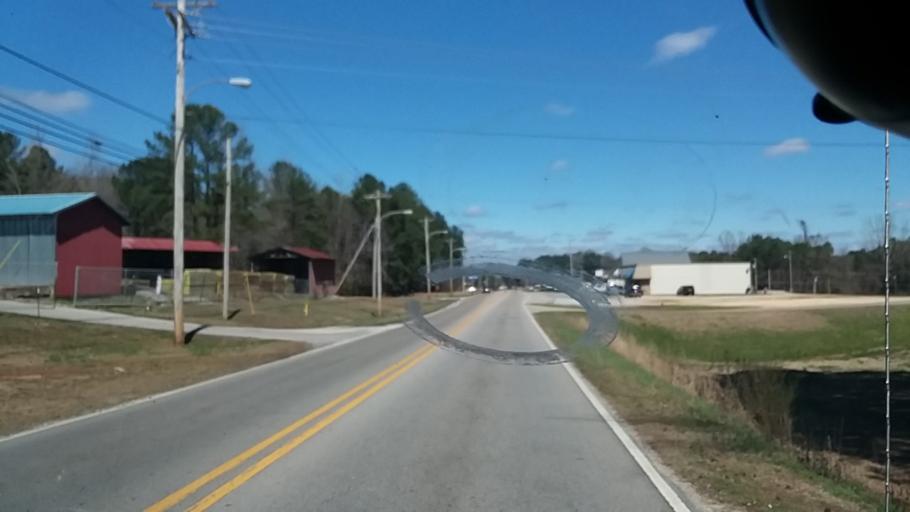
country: US
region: Mississippi
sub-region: Tishomingo County
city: Iuka
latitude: 34.8004
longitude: -88.2049
